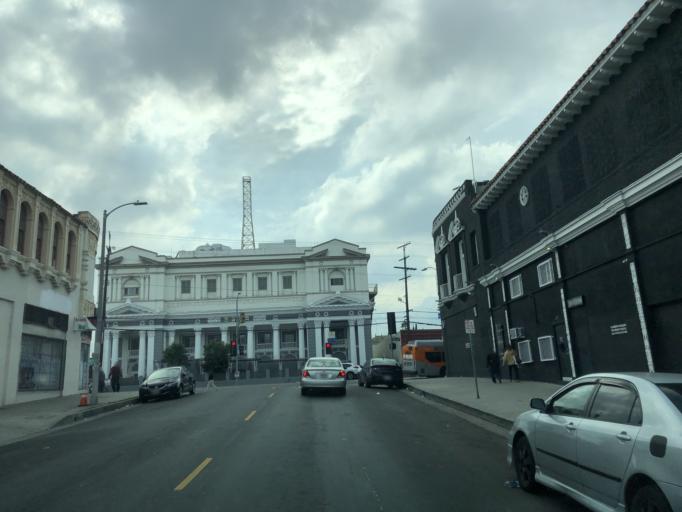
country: US
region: California
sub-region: Los Angeles County
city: Hollywood
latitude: 34.0480
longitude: -118.3237
